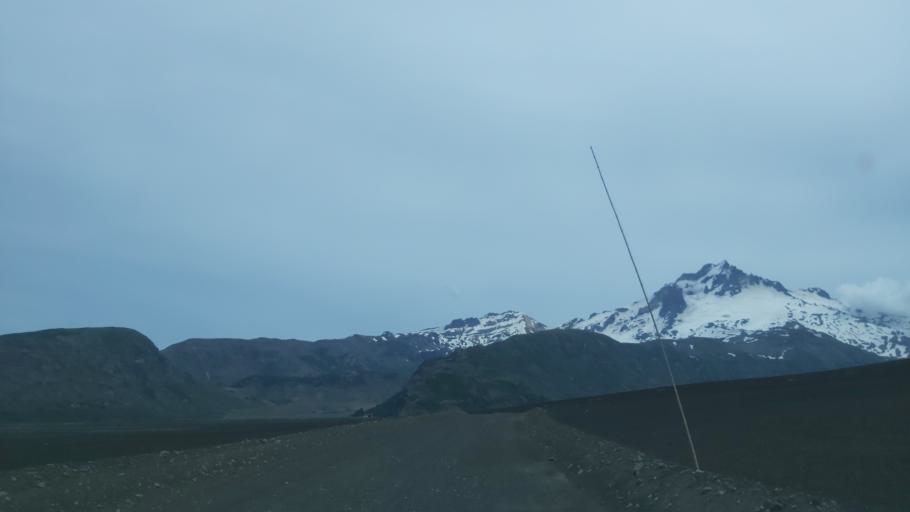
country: AR
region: Neuquen
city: Andacollo
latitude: -37.4570
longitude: -71.2974
